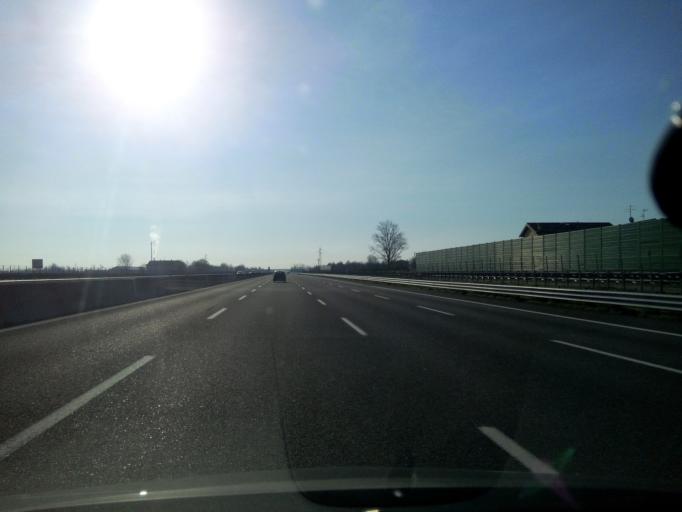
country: IT
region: Emilia-Romagna
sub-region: Provincia di Modena
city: Montale
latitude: 44.6053
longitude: 10.9154
